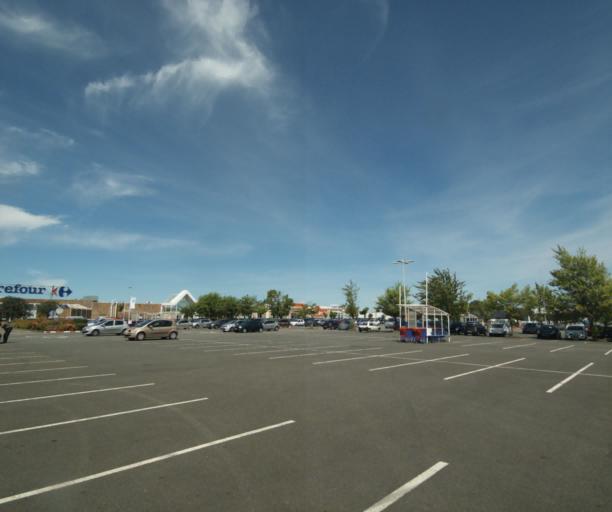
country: FR
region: Pays de la Loire
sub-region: Departement de la Mayenne
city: Change
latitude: 48.0786
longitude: -0.8006
